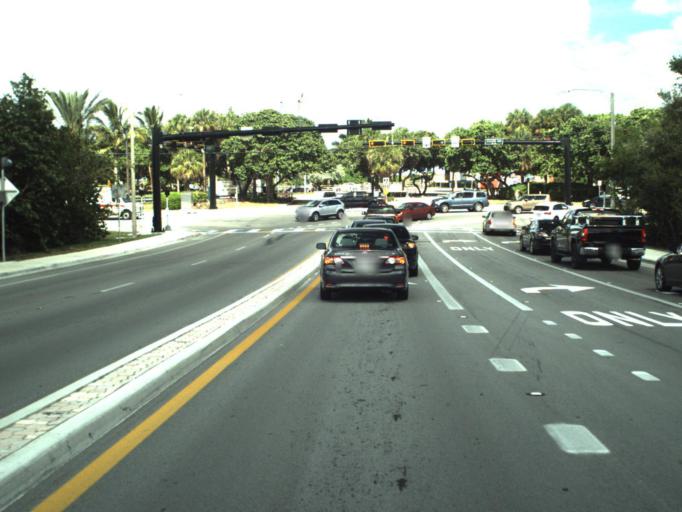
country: US
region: Florida
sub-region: Broward County
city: Dania Beach
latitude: 26.0343
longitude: -80.1163
